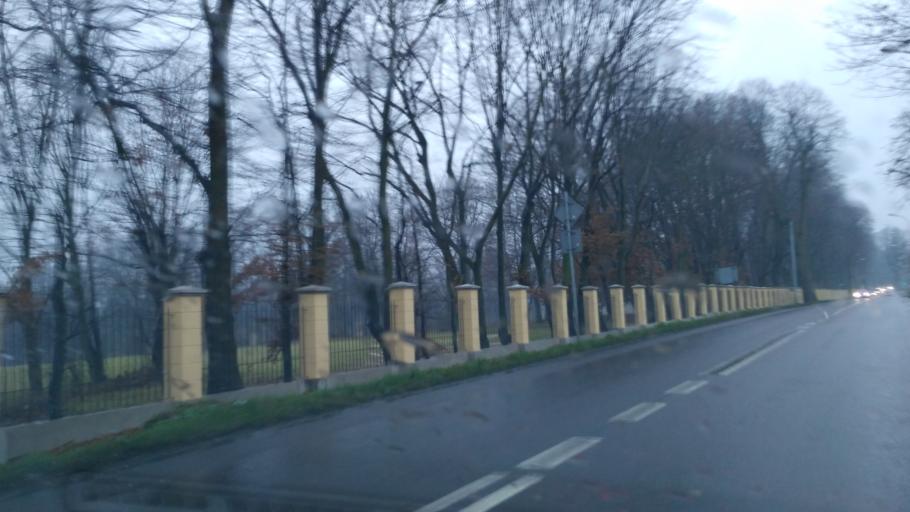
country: PL
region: Subcarpathian Voivodeship
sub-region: Powiat lancucki
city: Lancut
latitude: 50.0719
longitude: 22.2430
